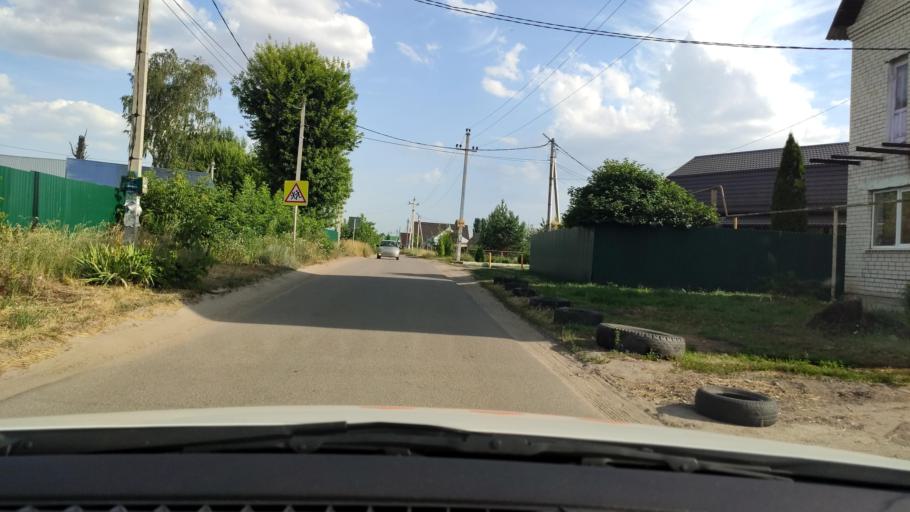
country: RU
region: Voronezj
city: Novaya Usman'
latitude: 51.6333
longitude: 39.4143
